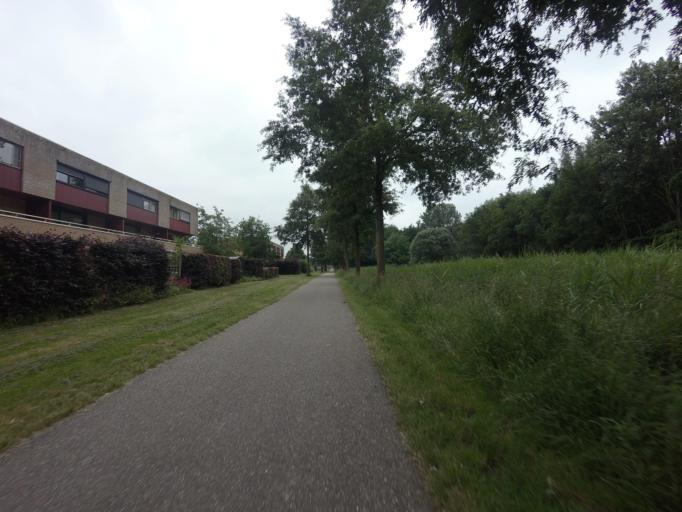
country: NL
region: Flevoland
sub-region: Gemeente Almere
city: Almere Stad
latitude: 52.4010
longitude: 5.2817
